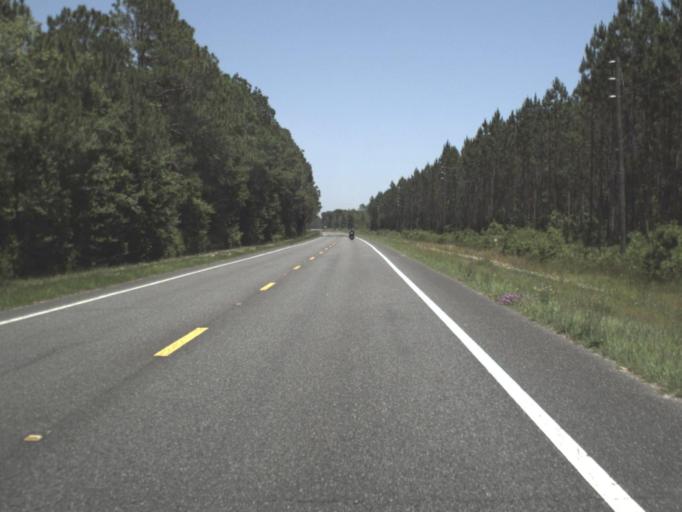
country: US
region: Florida
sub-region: Union County
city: Lake Butler
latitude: 30.2084
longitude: -82.4006
